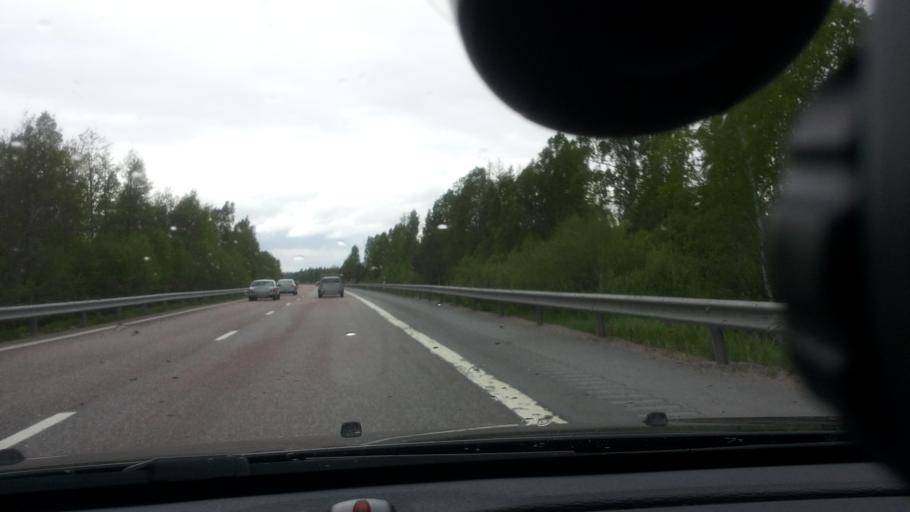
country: SE
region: Uppsala
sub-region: Alvkarleby Kommun
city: AElvkarleby
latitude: 60.4838
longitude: 17.3605
